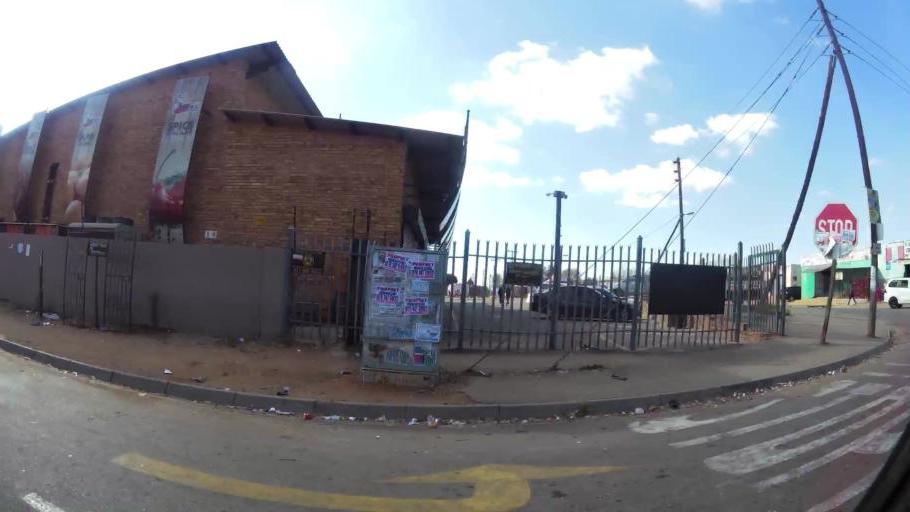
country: ZA
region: Gauteng
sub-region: West Rand District Municipality
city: Muldersdriseloop
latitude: -26.0235
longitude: 27.9239
